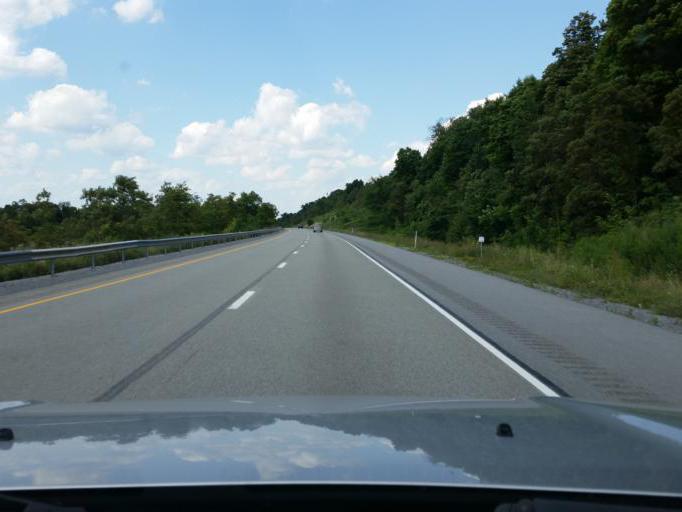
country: US
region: Pennsylvania
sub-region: Blair County
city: Claysburg
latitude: 40.2943
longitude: -78.4441
